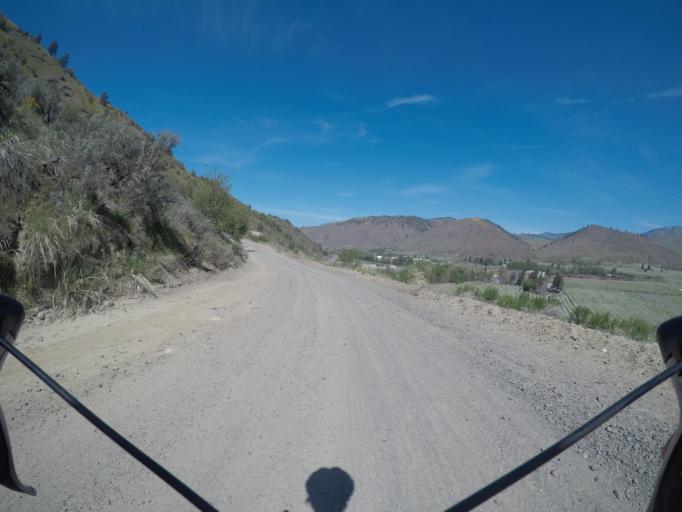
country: US
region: Washington
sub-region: Chelan County
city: Cashmere
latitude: 47.5050
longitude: -120.4460
